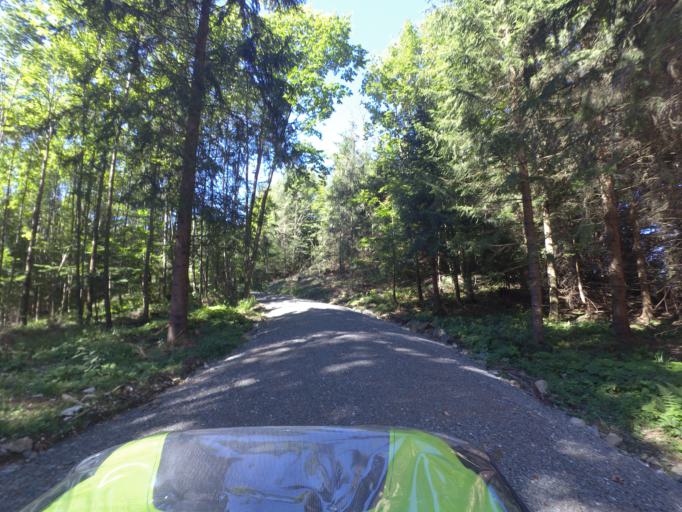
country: AT
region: Salzburg
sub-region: Politischer Bezirk Hallein
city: Hallein
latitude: 47.6537
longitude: 13.1015
